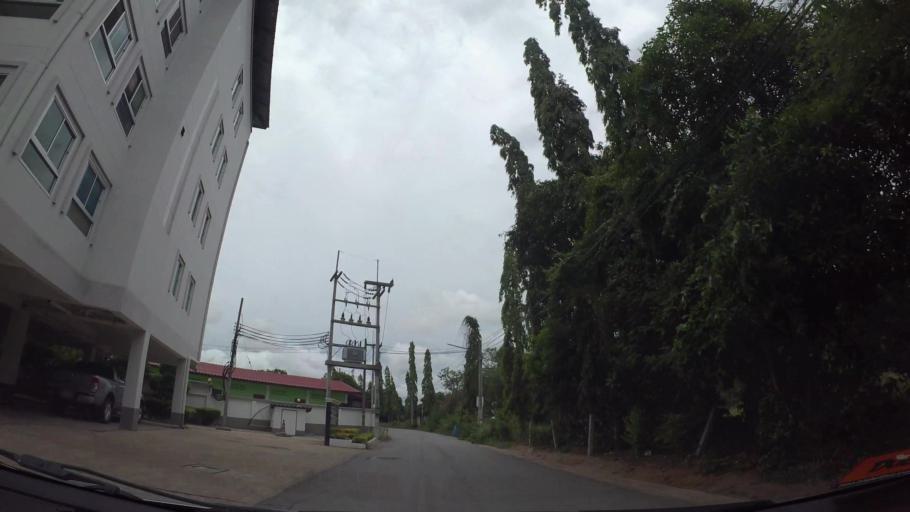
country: TH
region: Chon Buri
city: Sattahip
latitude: 12.7586
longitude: 100.8823
